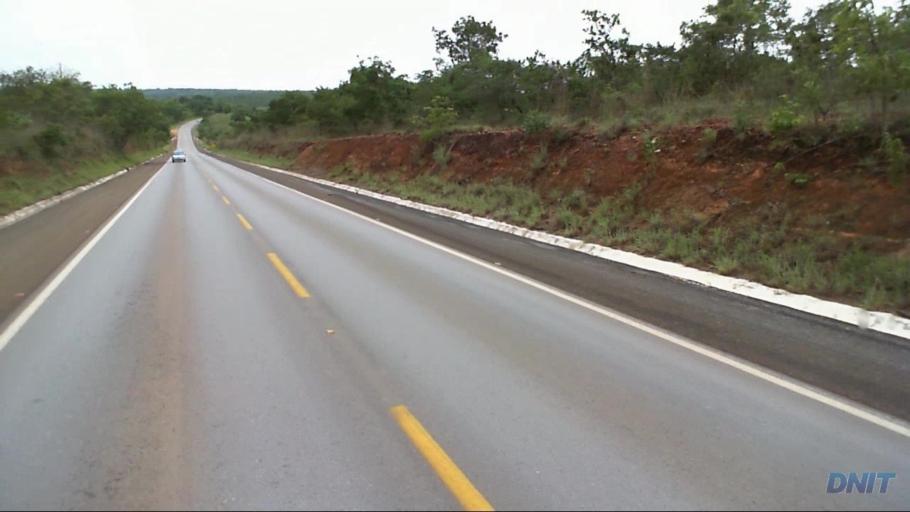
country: BR
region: Goias
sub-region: Uruacu
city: Uruacu
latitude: -14.7554
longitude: -49.0692
